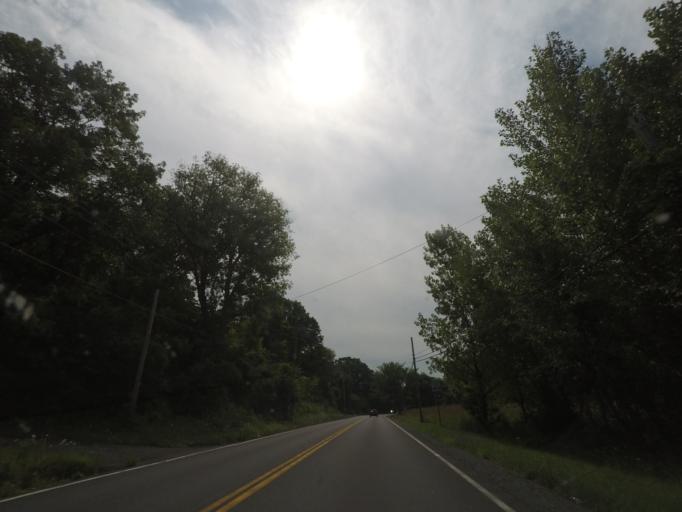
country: US
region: New York
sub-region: Saratoga County
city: Waterford
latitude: 42.7632
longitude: -73.6234
